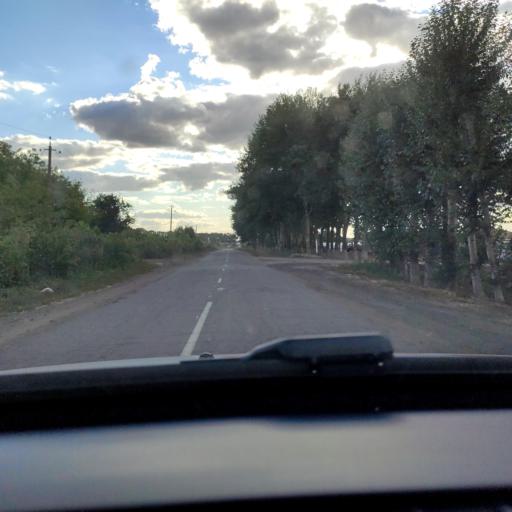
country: RU
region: Voronezj
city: Verkhnyaya Khava
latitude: 51.6132
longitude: 39.8158
